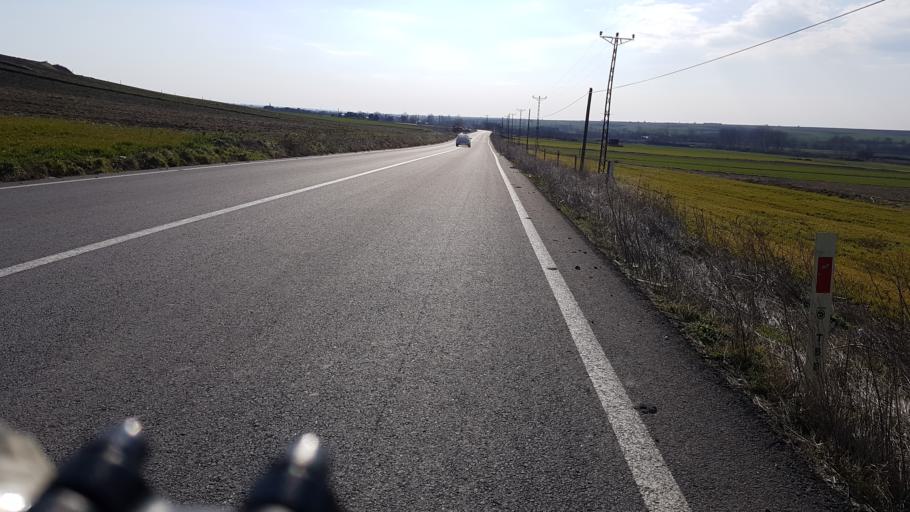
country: TR
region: Tekirdag
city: Velimese
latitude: 41.3532
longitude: 27.8446
